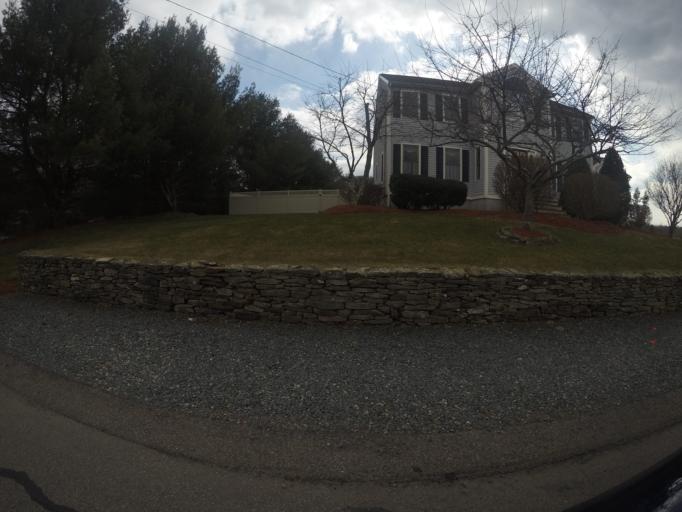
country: US
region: Massachusetts
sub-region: Bristol County
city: Easton
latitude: 42.0566
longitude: -71.1337
